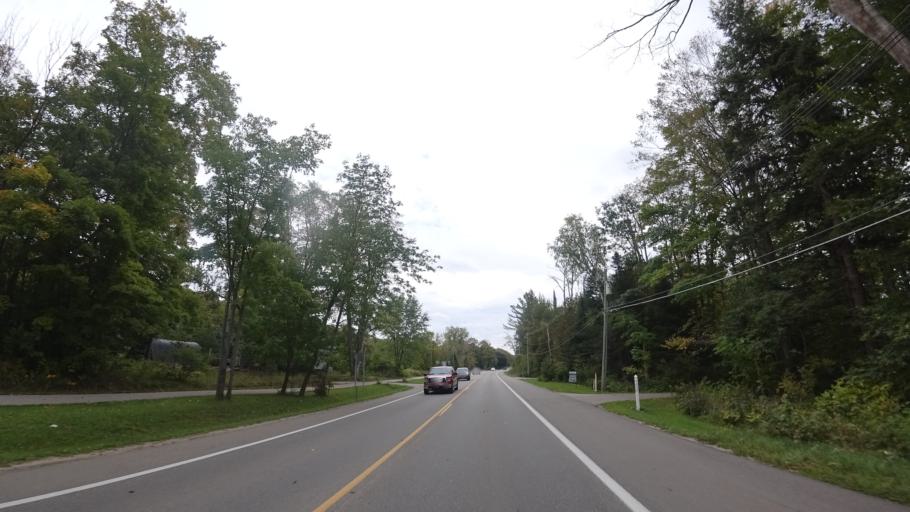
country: US
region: Michigan
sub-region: Emmet County
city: Harbor Springs
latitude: 45.4314
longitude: -84.9358
